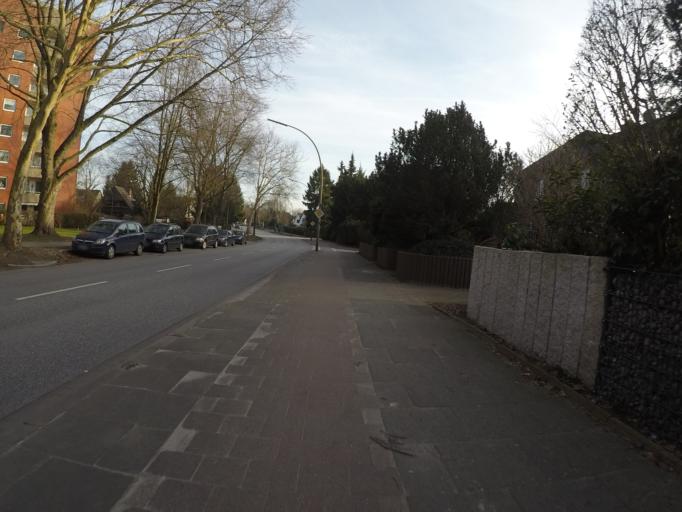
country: DE
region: Schleswig-Holstein
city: Halstenbek
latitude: 53.5968
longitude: 9.8496
